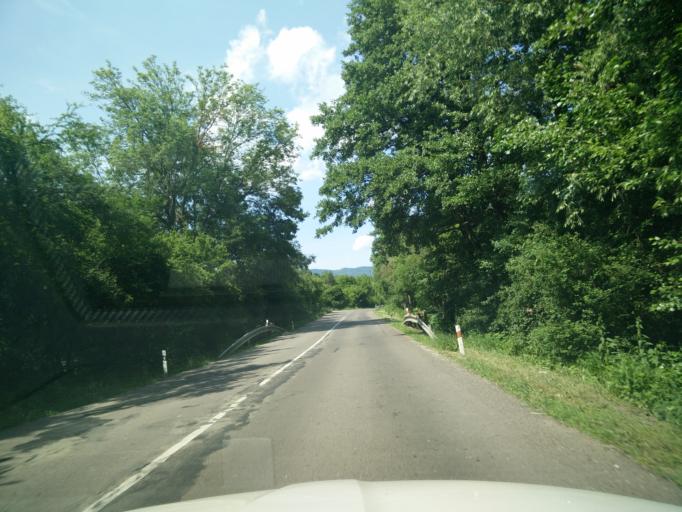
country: SK
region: Nitriansky
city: Prievidza
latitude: 48.8864
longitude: 18.6384
